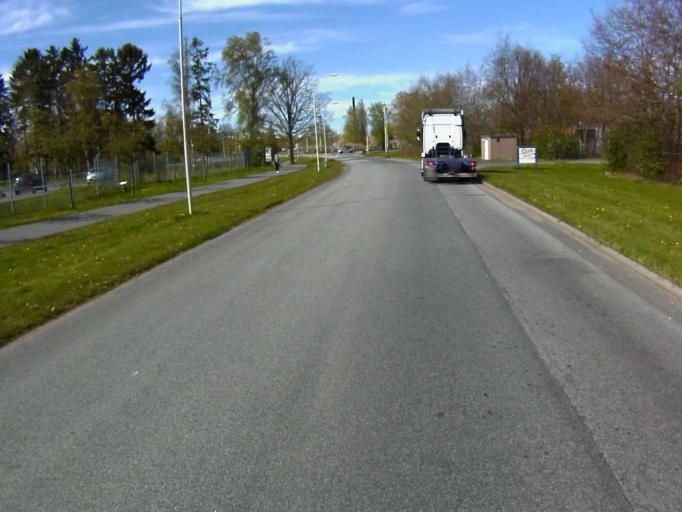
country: SE
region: Skane
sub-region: Kristianstads Kommun
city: Kristianstad
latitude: 56.0416
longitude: 14.1521
